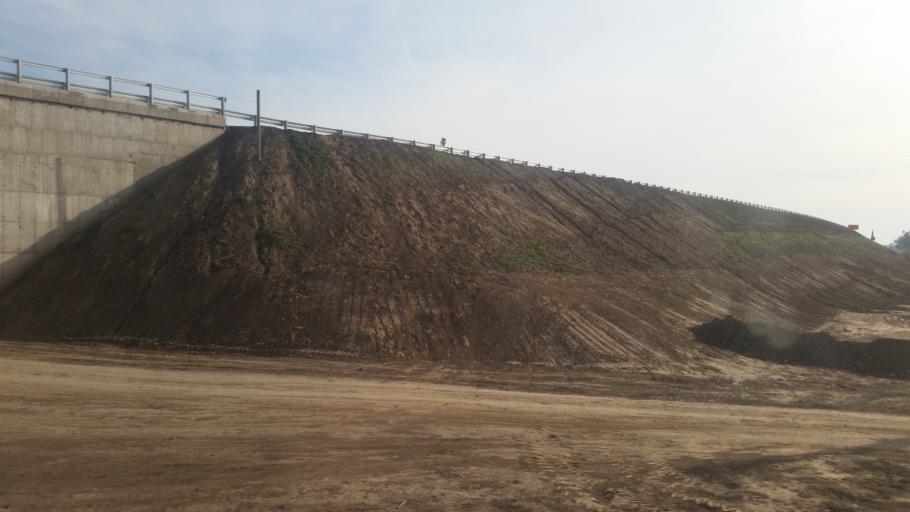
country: AR
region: Cordoba
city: Bell Ville
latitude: -32.6152
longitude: -62.7161
